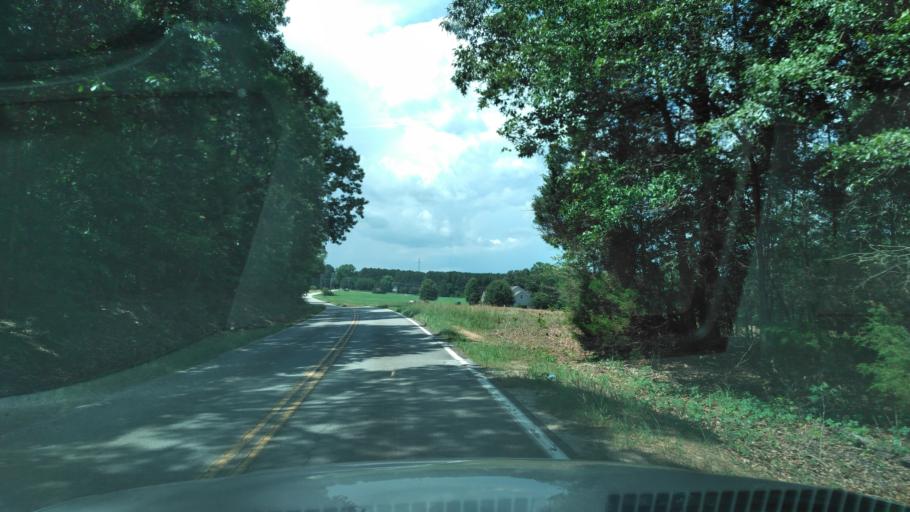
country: US
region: South Carolina
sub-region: Laurens County
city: Laurens
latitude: 34.4993
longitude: -82.0942
